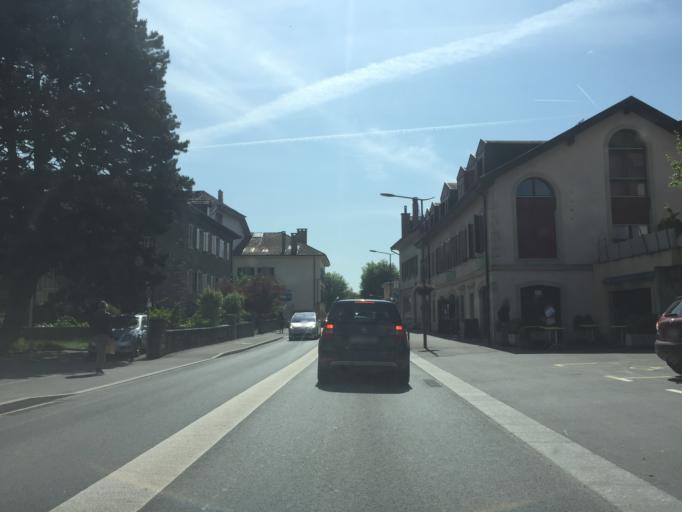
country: CH
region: Vaud
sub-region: Morges District
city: Cossonay
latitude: 46.6139
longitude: 6.5075
